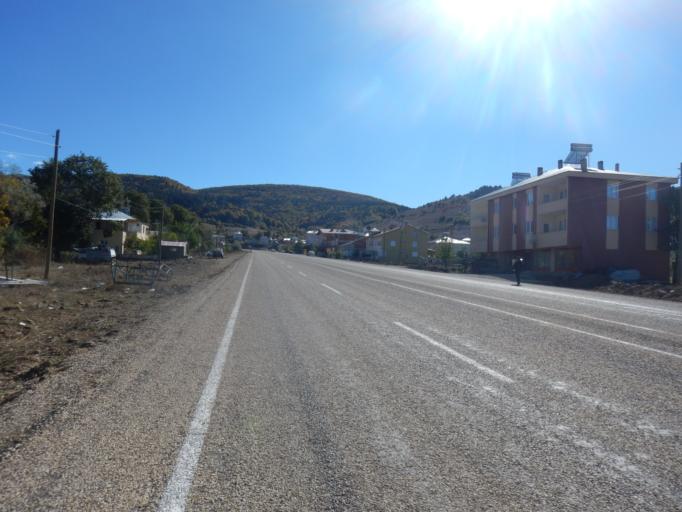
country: TR
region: Ordu
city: Mesudiye
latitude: 40.4380
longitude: 37.7732
